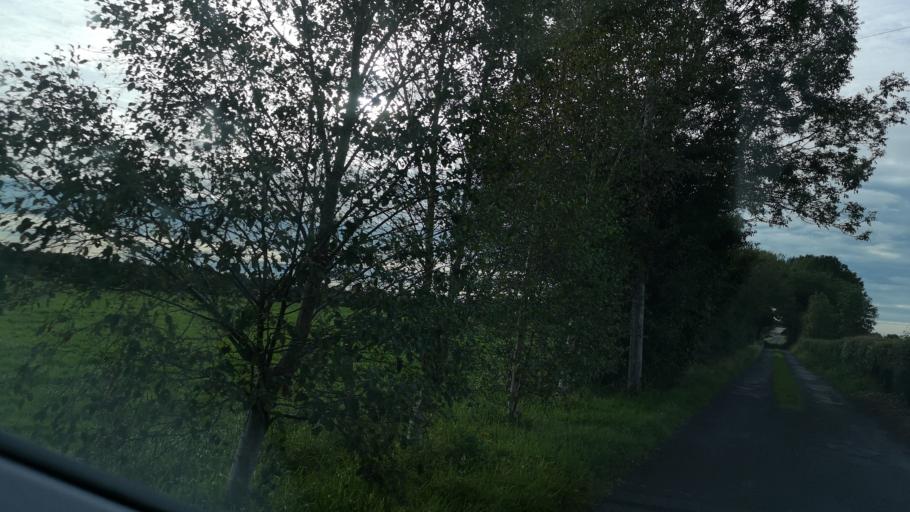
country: IE
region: Connaught
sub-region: County Galway
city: Ballinasloe
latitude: 53.3416
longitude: -8.2697
